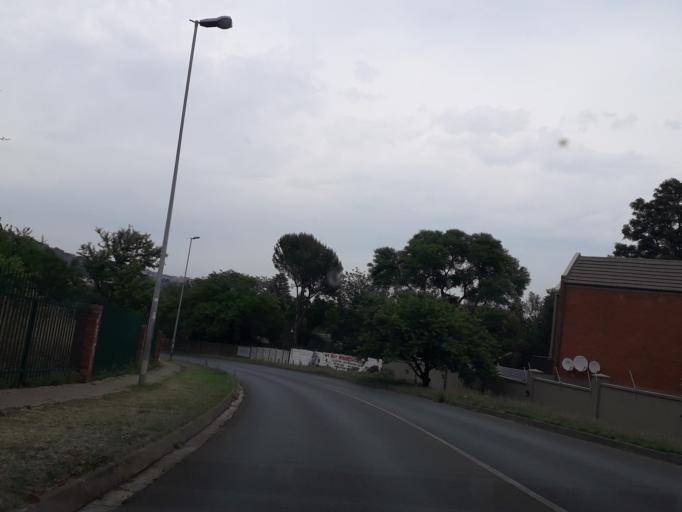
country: ZA
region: Gauteng
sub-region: City of Johannesburg Metropolitan Municipality
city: Johannesburg
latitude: -26.1275
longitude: 27.9804
